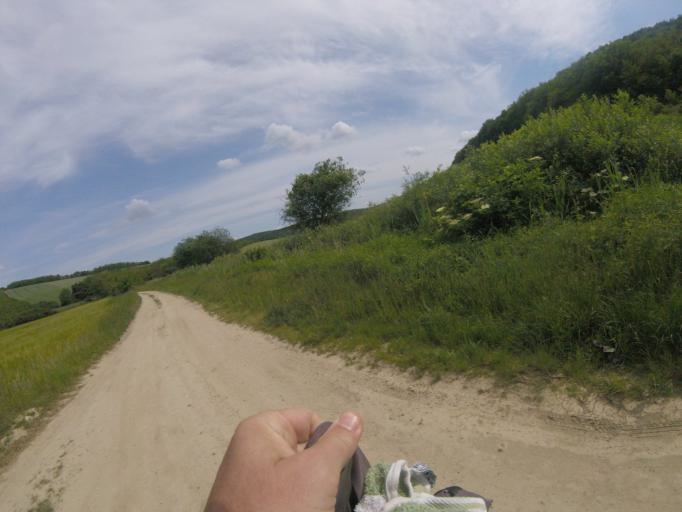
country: HU
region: Zala
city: Zalaszentgrot
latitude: 46.8928
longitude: 17.0550
